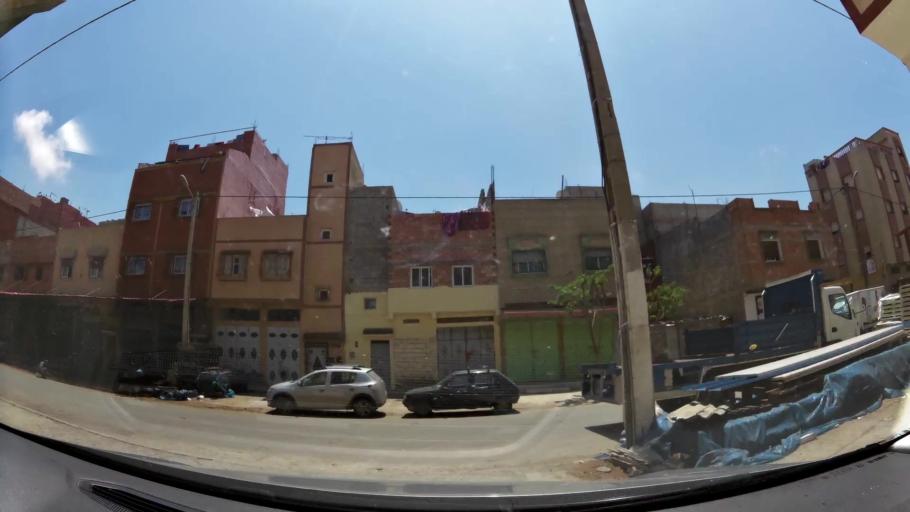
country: MA
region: Rabat-Sale-Zemmour-Zaer
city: Sale
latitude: 34.0699
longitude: -6.7852
